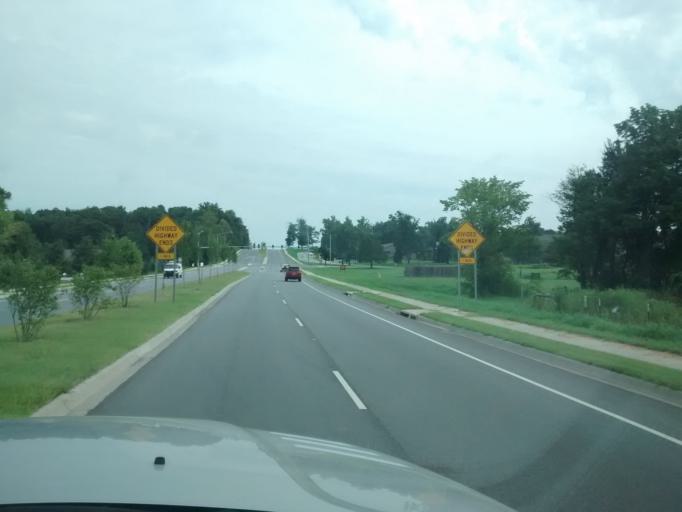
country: US
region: Arkansas
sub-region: Washington County
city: Johnson
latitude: 36.1343
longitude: -94.1178
